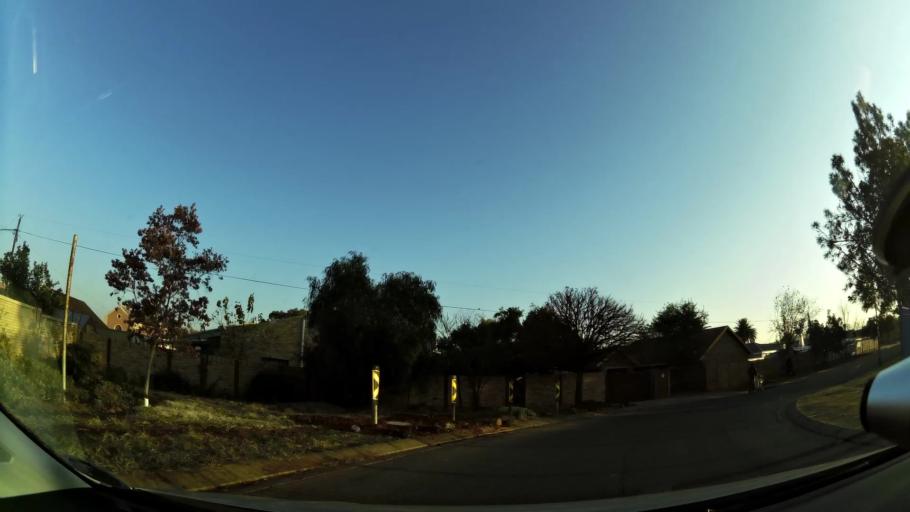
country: ZA
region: Orange Free State
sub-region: Mangaung Metropolitan Municipality
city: Bloemfontein
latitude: -29.0863
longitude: 26.1614
